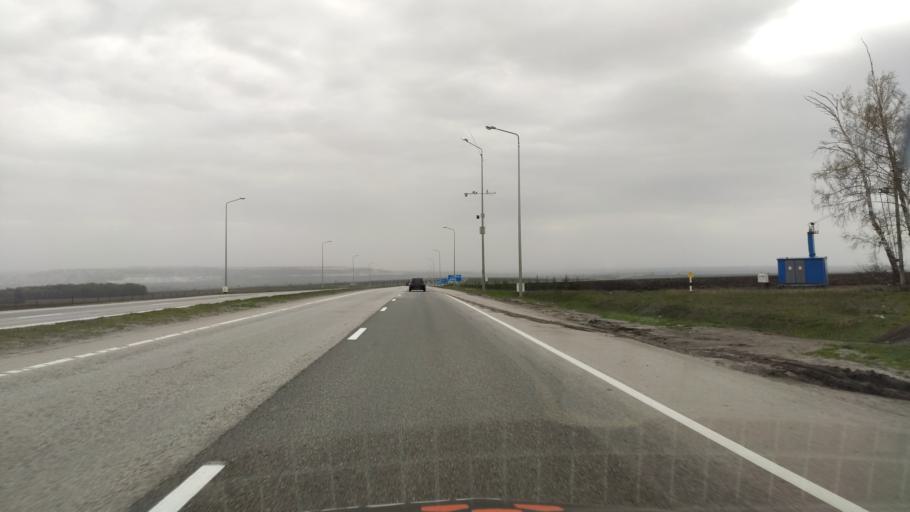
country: RU
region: Belgorod
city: Staryy Oskol
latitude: 51.3316
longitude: 37.7536
